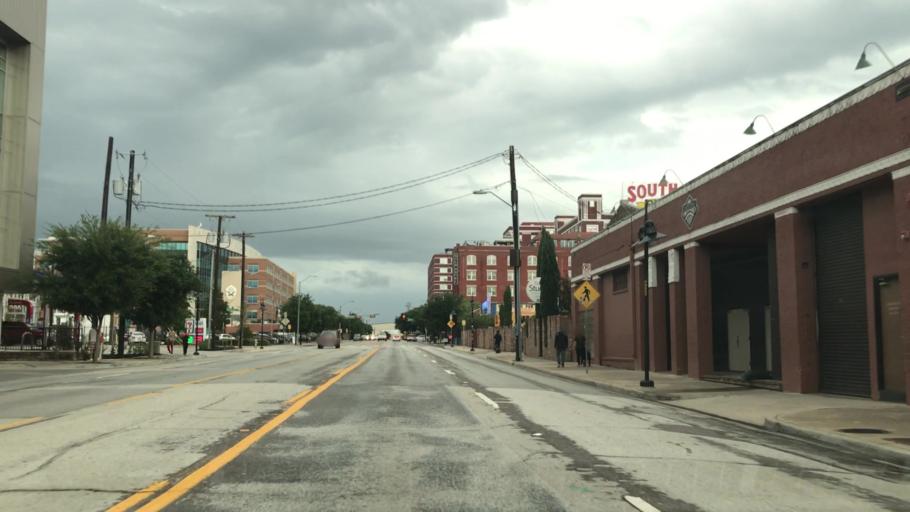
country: US
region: Texas
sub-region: Dallas County
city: Dallas
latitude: 32.7691
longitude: -96.7975
